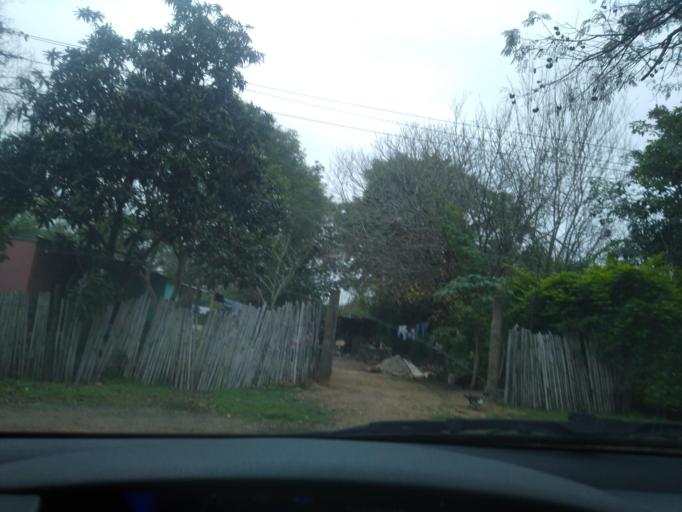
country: AR
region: Chaco
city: Colonia Benitez
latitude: -27.3330
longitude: -58.9573
